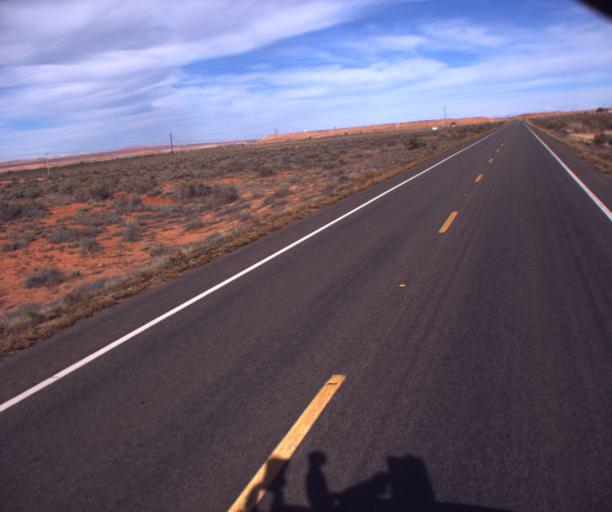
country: US
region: Arizona
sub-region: Navajo County
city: Kayenta
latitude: 36.8113
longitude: -109.8989
